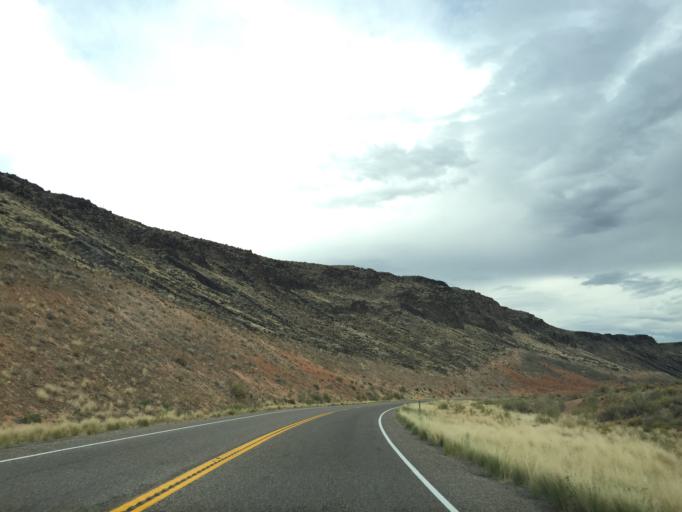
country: US
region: Utah
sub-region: Washington County
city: LaVerkin
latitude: 37.1952
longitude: -113.1494
